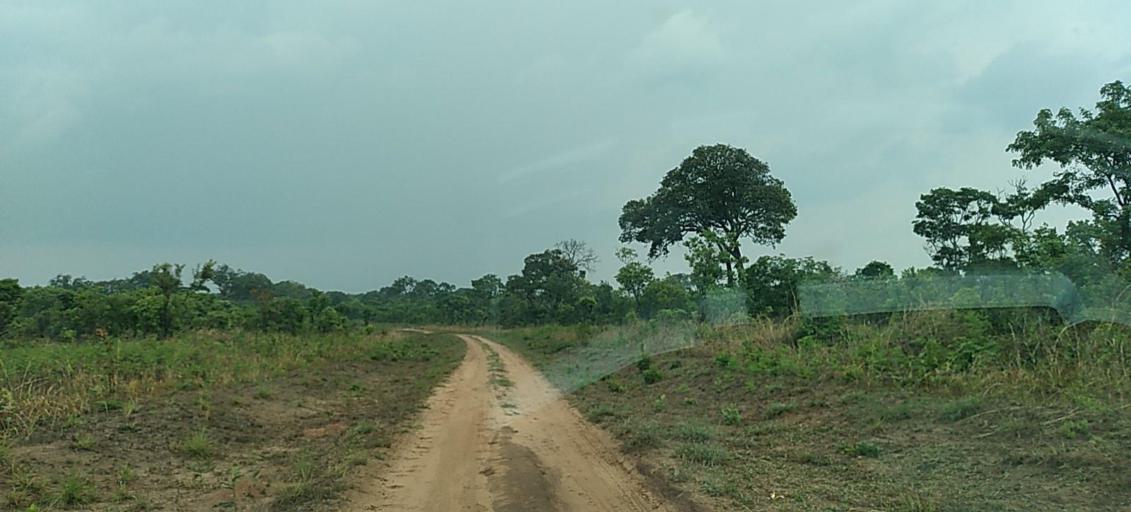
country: ZM
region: North-Western
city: Mwinilunga
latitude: -11.4441
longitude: 24.5916
